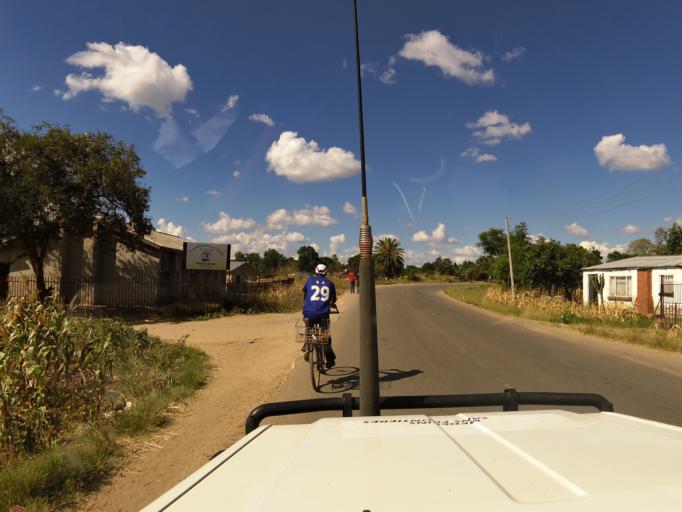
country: ZW
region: Harare
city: Epworth
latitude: -17.8773
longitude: 31.1261
